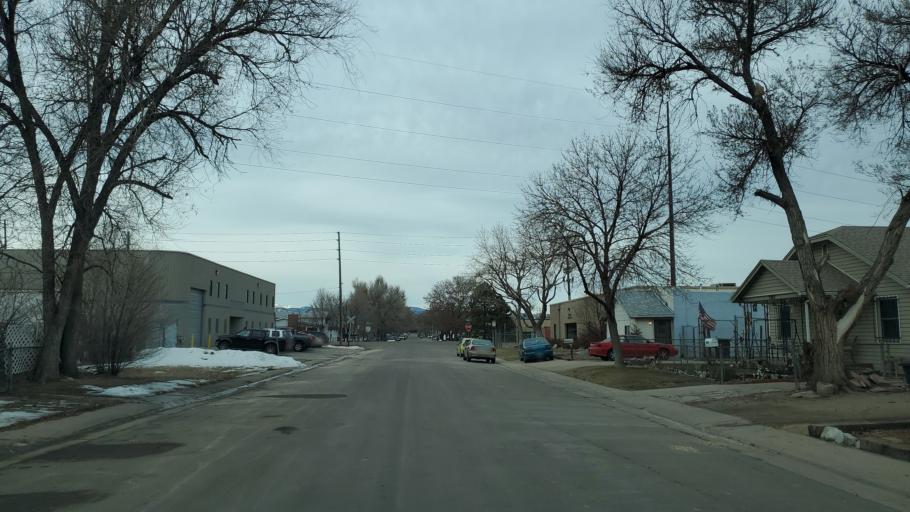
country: US
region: Colorado
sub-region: Denver County
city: Denver
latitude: 39.7122
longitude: -105.0027
